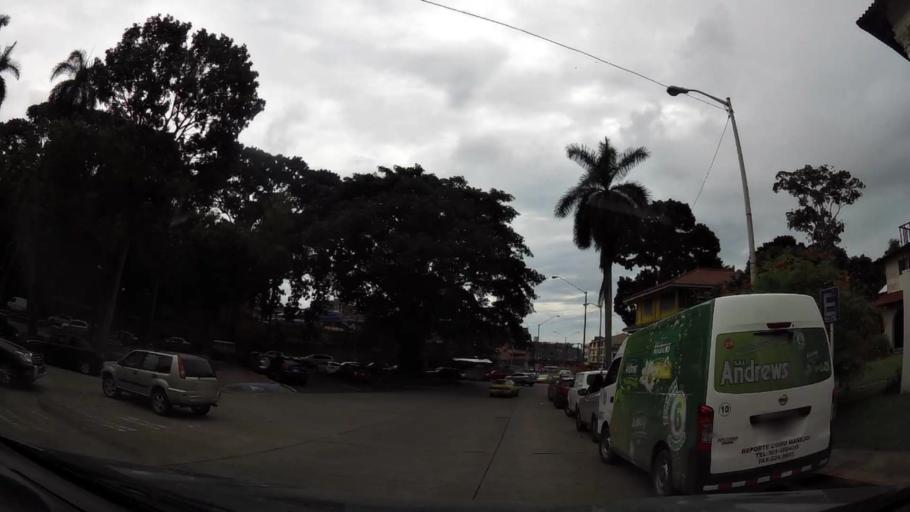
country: PA
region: Panama
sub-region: Distrito de Panama
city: Ancon
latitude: 8.9597
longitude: -79.5440
